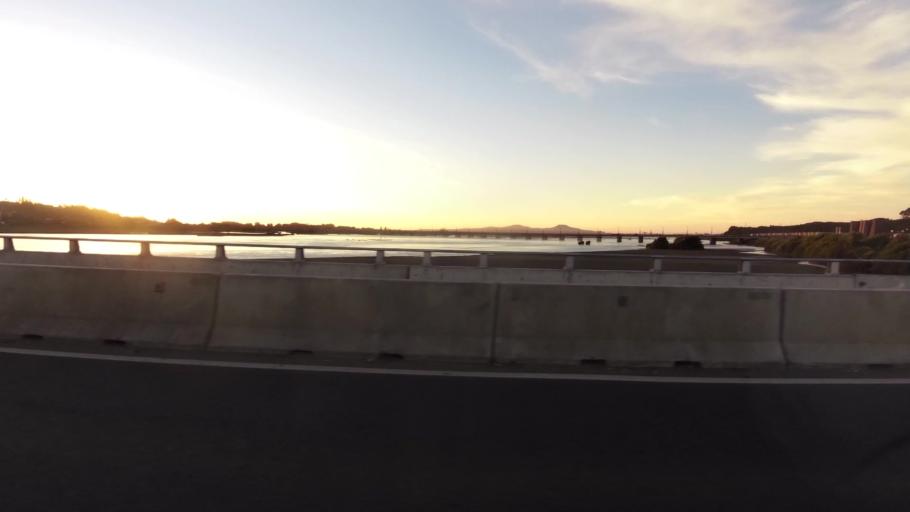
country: CL
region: Biobio
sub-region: Provincia de Concepcion
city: Concepcion
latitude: -36.8365
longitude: -73.0640
